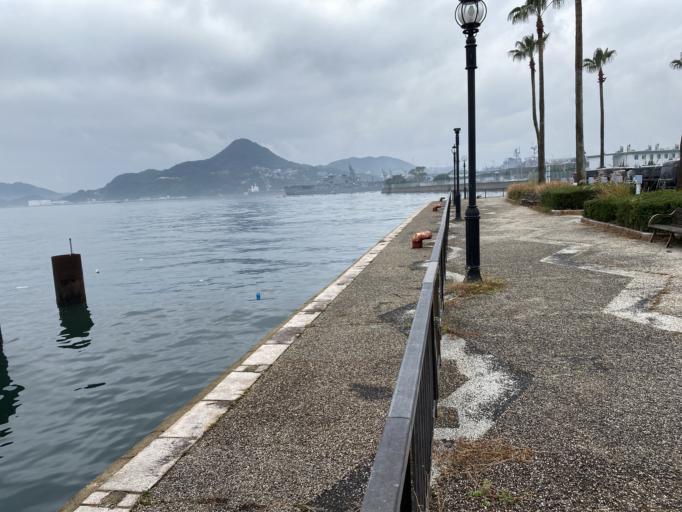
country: JP
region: Nagasaki
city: Sasebo
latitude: 33.1620
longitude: 129.7228
